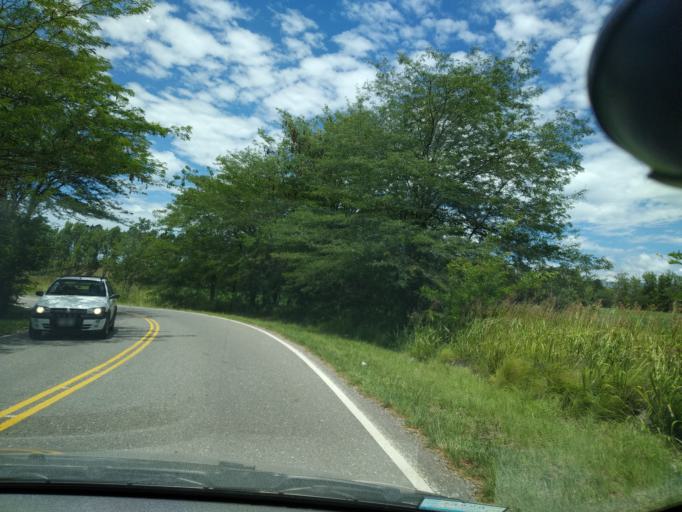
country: AR
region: Cordoba
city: Cuesta Blanca
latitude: -31.6037
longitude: -64.5626
